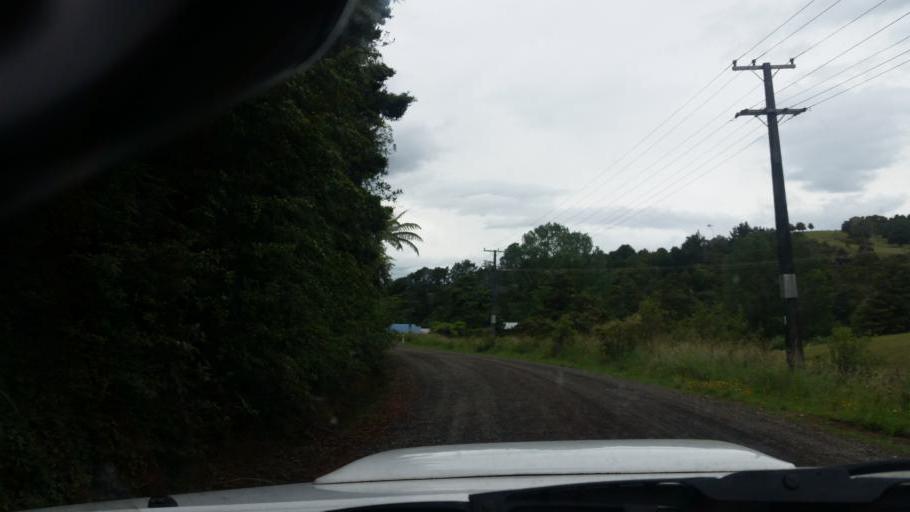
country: NZ
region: Northland
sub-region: Kaipara District
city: Dargaville
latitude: -35.7111
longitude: 173.6170
